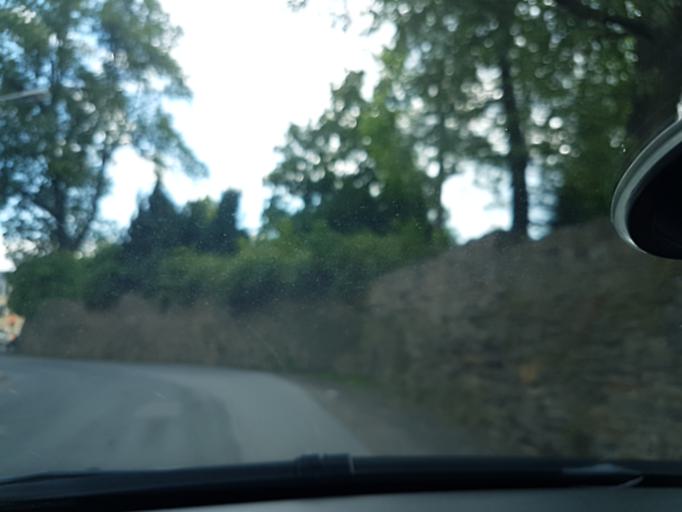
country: DE
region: Saxony
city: Freiberg
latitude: 50.9137
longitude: 13.3335
